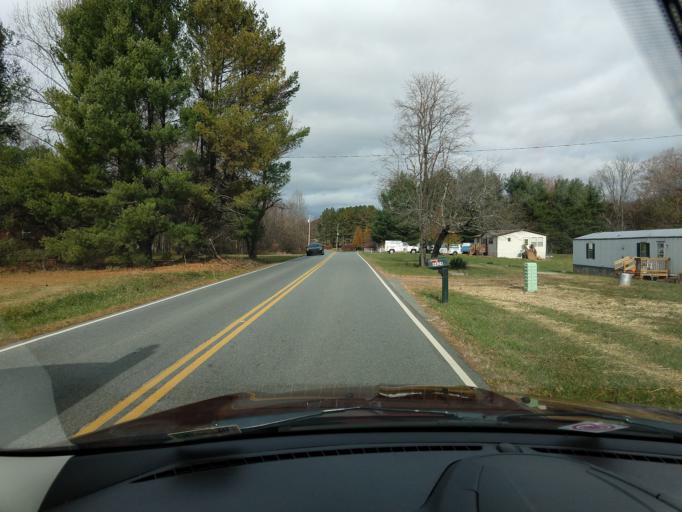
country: US
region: Virginia
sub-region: Franklin County
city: North Shore
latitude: 37.1716
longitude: -79.6366
